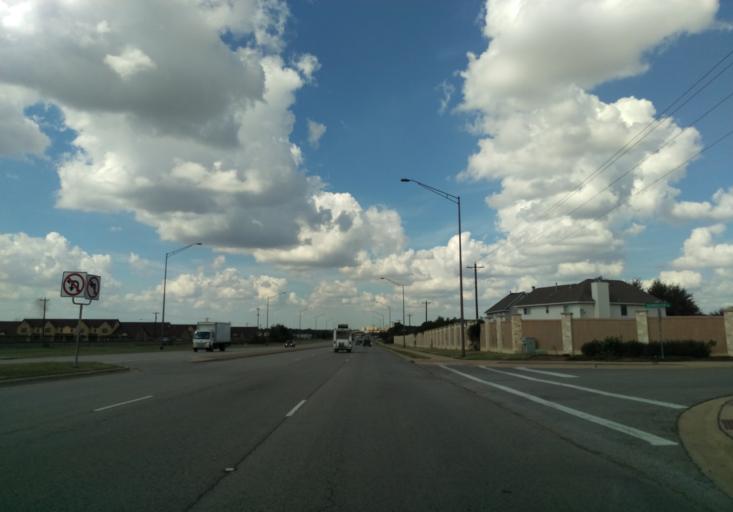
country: US
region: Texas
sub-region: Brazos County
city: College Station
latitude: 30.5732
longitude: -96.3128
